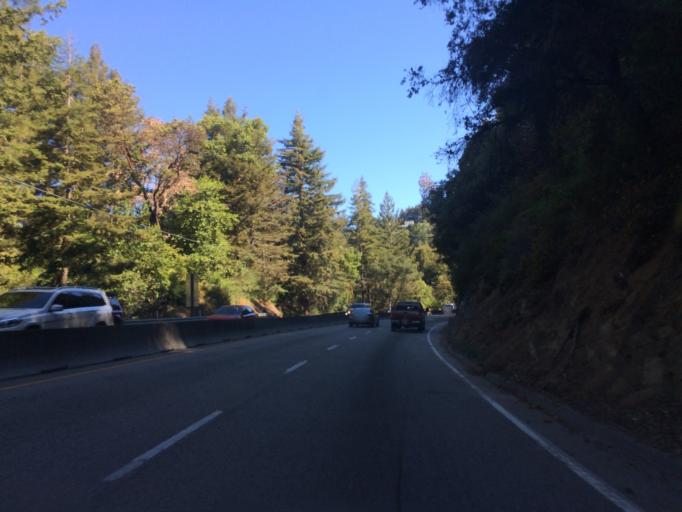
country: US
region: California
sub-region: Santa Cruz County
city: Scotts Valley
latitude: 37.0918
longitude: -121.9784
